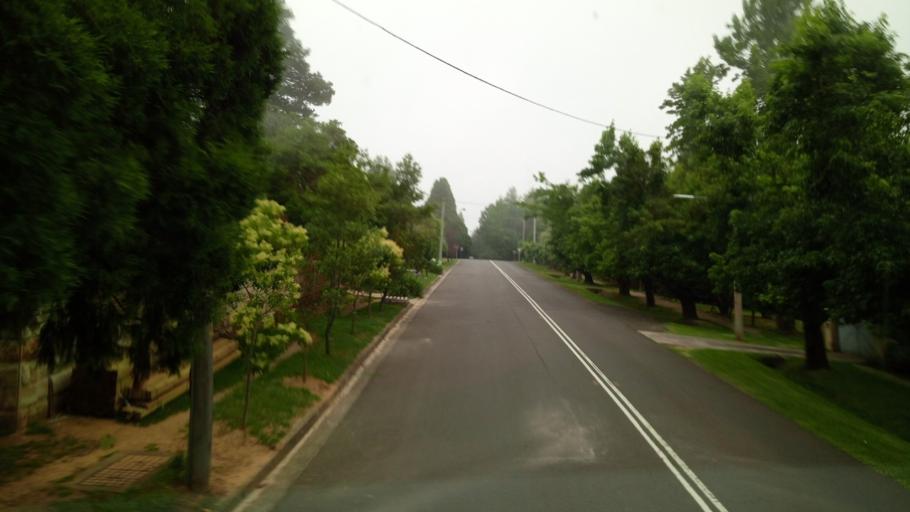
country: AU
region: New South Wales
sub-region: Blue Mountains Municipality
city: Leura
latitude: -33.7196
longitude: 150.3413
